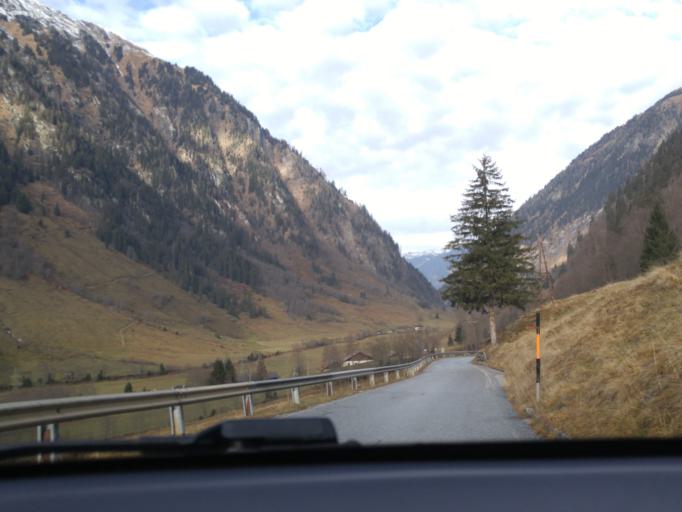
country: AT
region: Salzburg
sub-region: Politischer Bezirk Zell am See
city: Uttendorf
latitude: 47.2026
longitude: 12.6035
